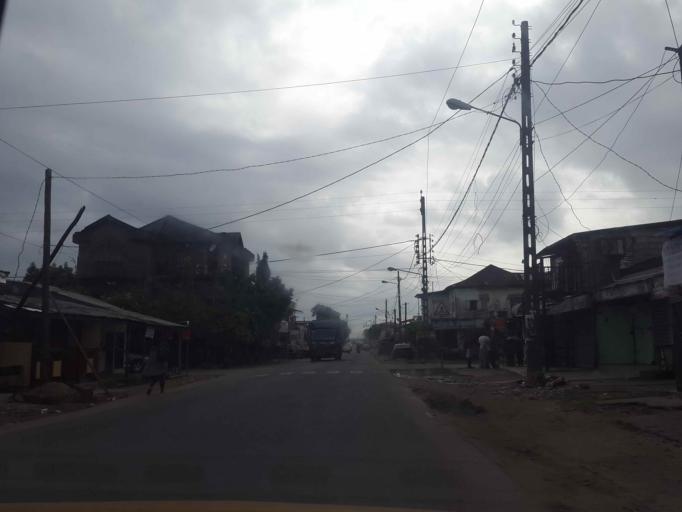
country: CM
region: Littoral
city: Douala
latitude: 4.0678
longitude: 9.7107
